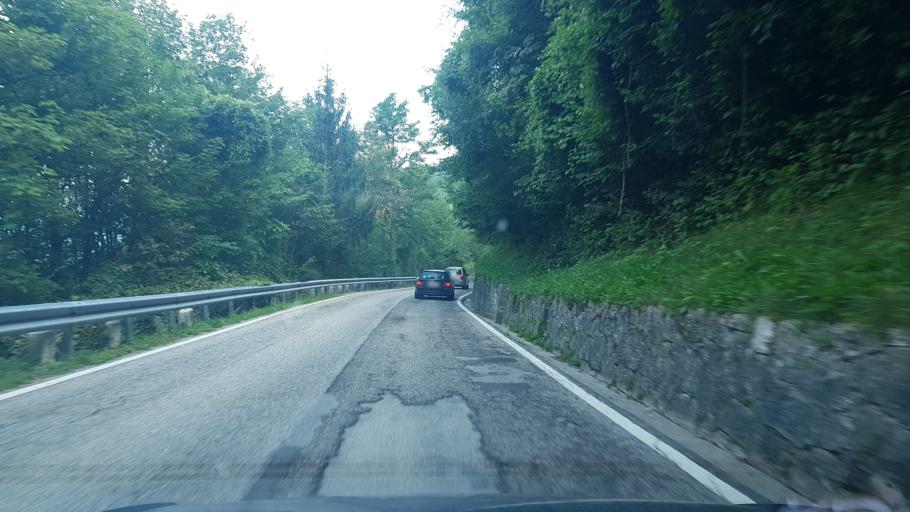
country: IT
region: Veneto
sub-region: Provincia di Vicenza
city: Recoaro Terme
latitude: 45.7602
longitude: 11.2035
